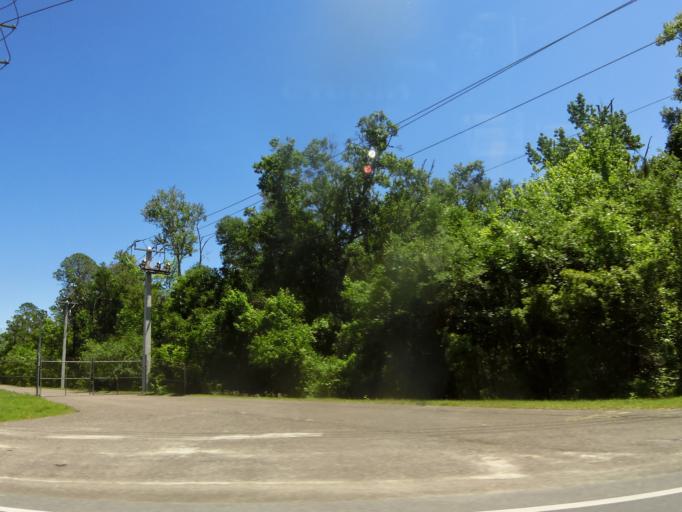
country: US
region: Florida
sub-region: Clay County
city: Green Cove Springs
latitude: 30.0201
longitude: -81.6003
